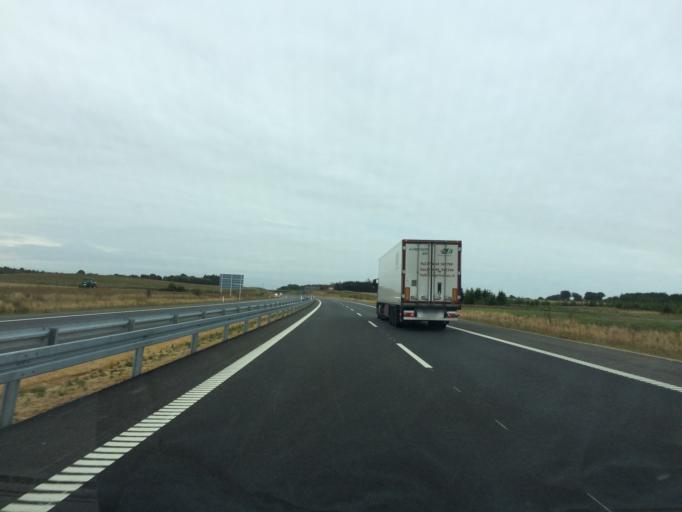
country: DK
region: Central Jutland
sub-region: Herning Kommune
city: Snejbjerg
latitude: 56.1418
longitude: 8.8692
